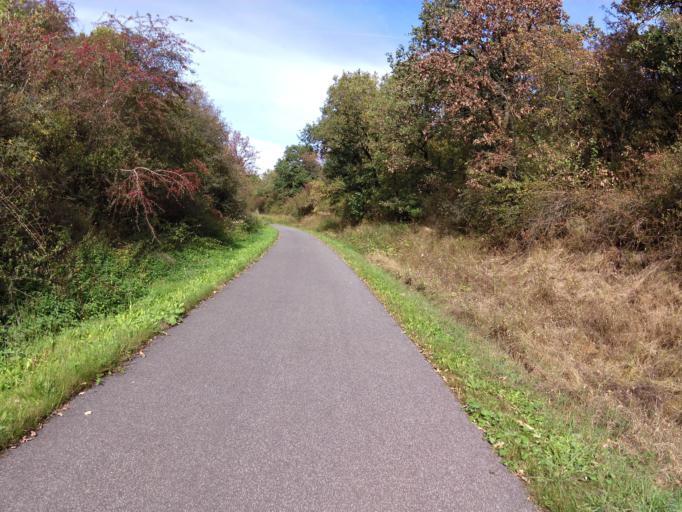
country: DE
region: Rheinland-Pfalz
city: Strickscheid
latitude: 50.1328
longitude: 6.3206
